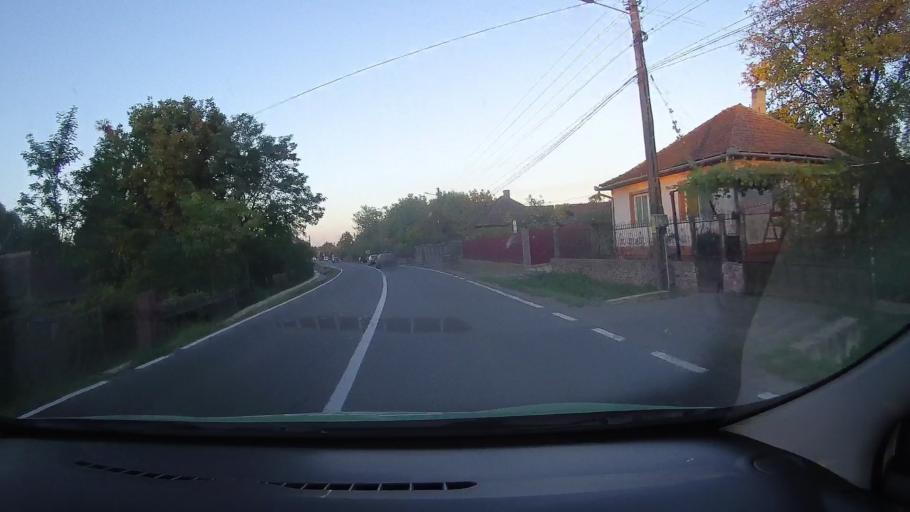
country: RO
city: Szekelyhid
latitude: 47.3327
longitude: 22.0863
